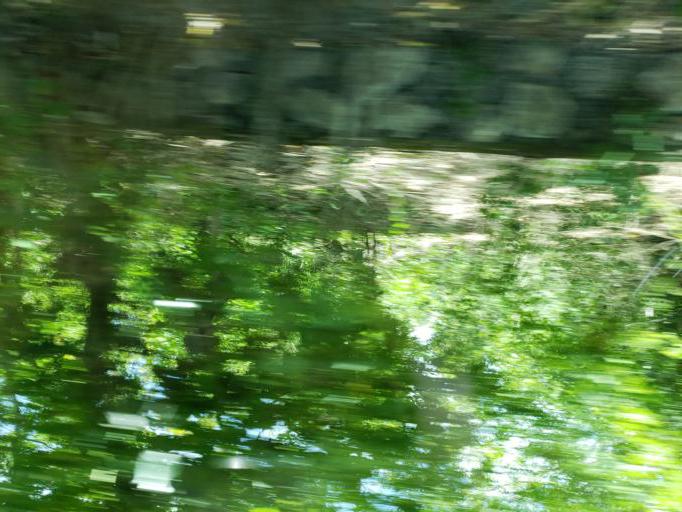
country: ID
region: Bali
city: Kangin
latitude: -8.8390
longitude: 115.1373
